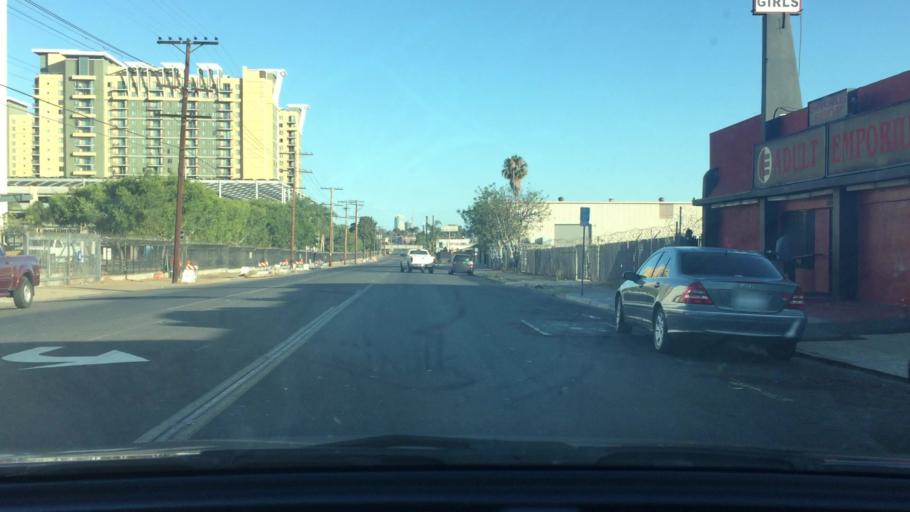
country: US
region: California
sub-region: San Diego County
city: National City
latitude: 32.6868
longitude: -117.1173
